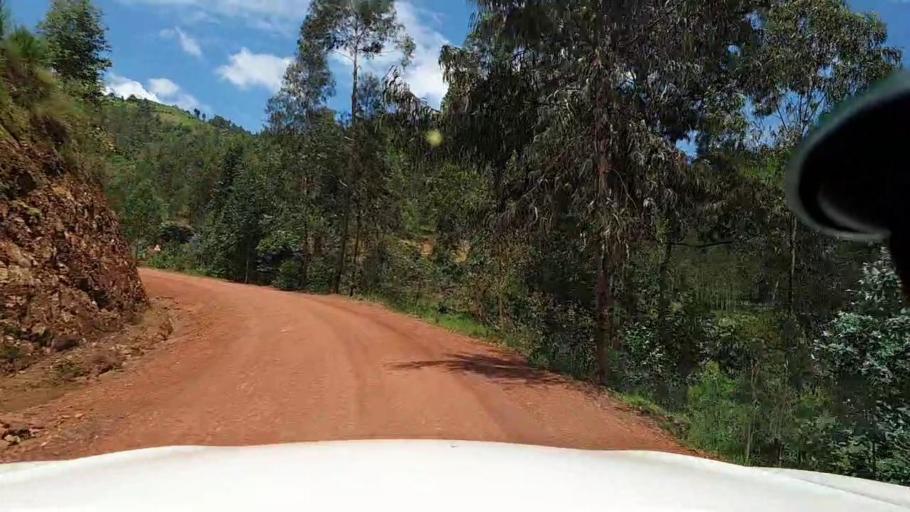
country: RW
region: Northern Province
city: Byumba
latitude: -1.7413
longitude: 29.8619
